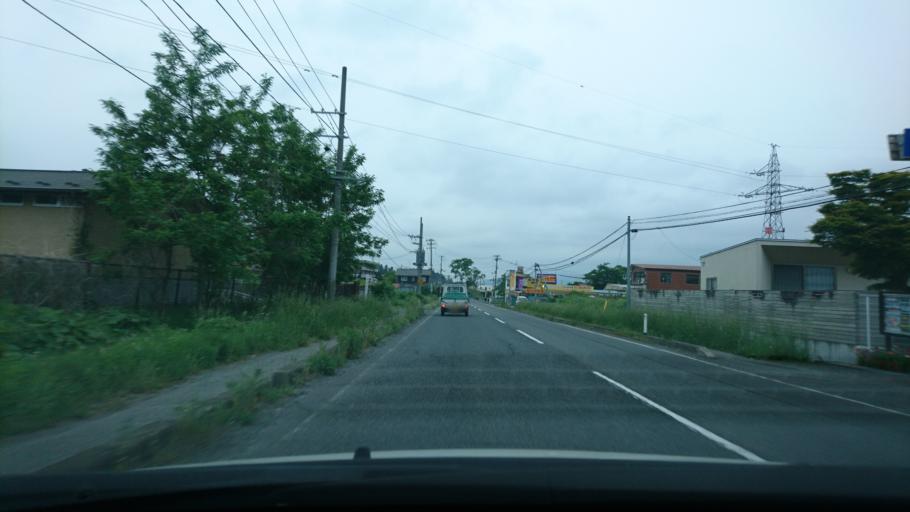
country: JP
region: Iwate
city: Ichinoseki
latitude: 38.9109
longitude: 141.1312
